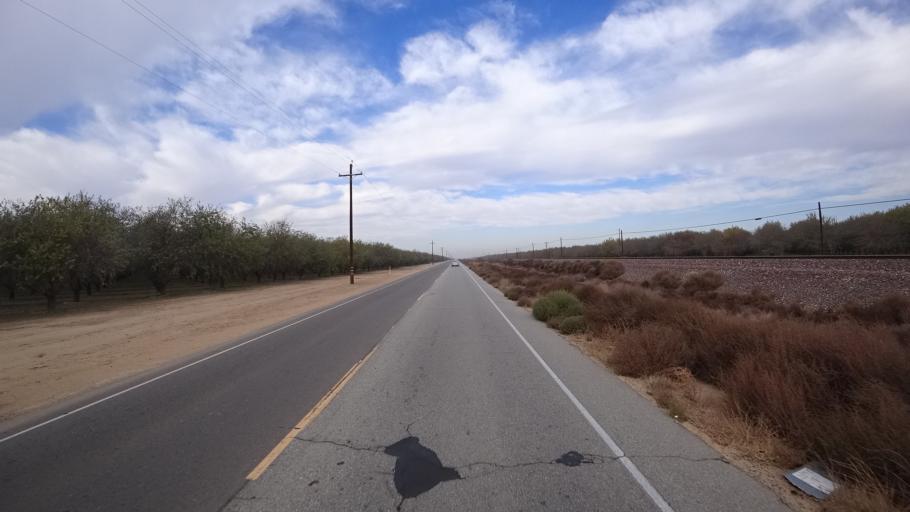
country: US
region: California
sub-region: Kern County
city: Rosedale
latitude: 35.4223
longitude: -119.1755
